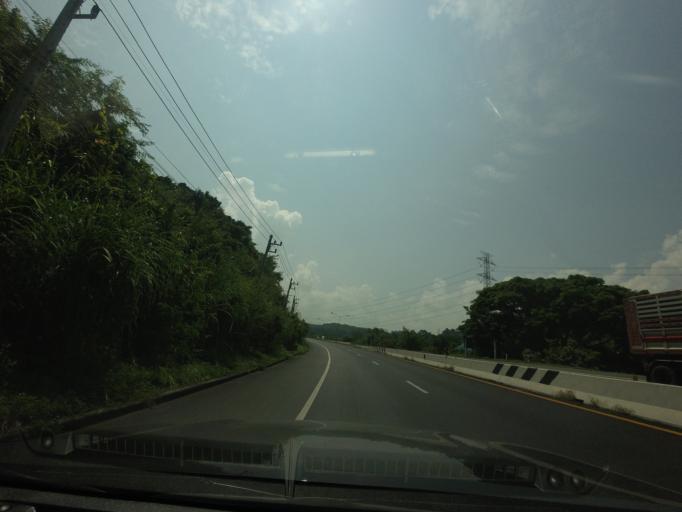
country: TH
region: Phrae
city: Den Chai
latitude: 17.8918
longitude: 100.0484
